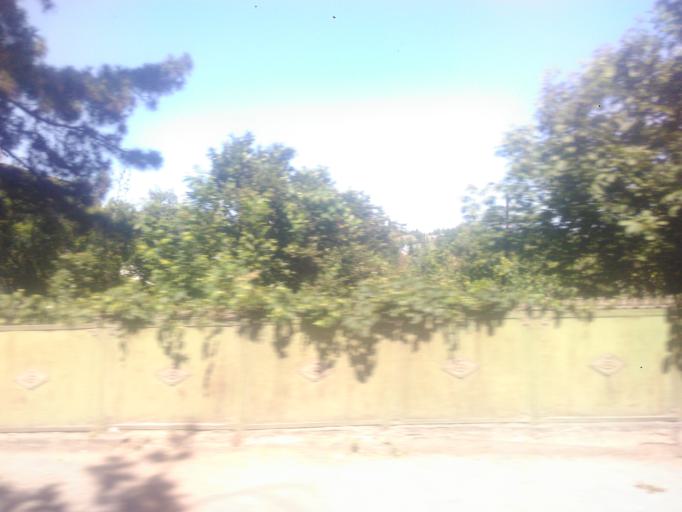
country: GE
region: T'bilisi
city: Tbilisi
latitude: 41.6929
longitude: 44.8919
